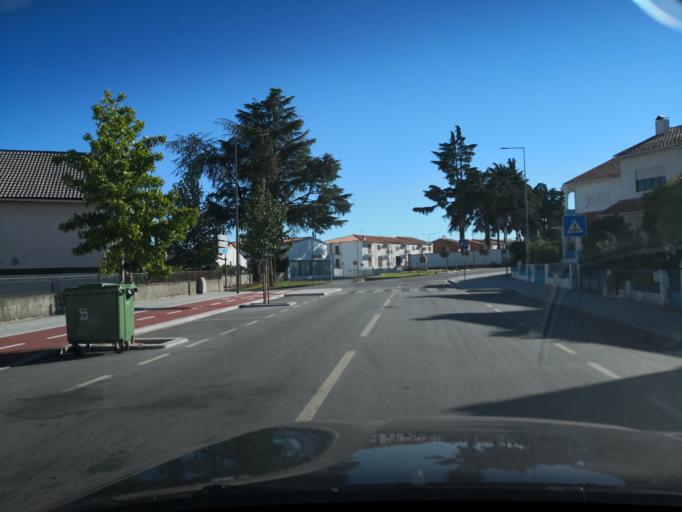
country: PT
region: Vila Real
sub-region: Valpacos
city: Valpacos
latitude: 41.6058
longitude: -7.3135
